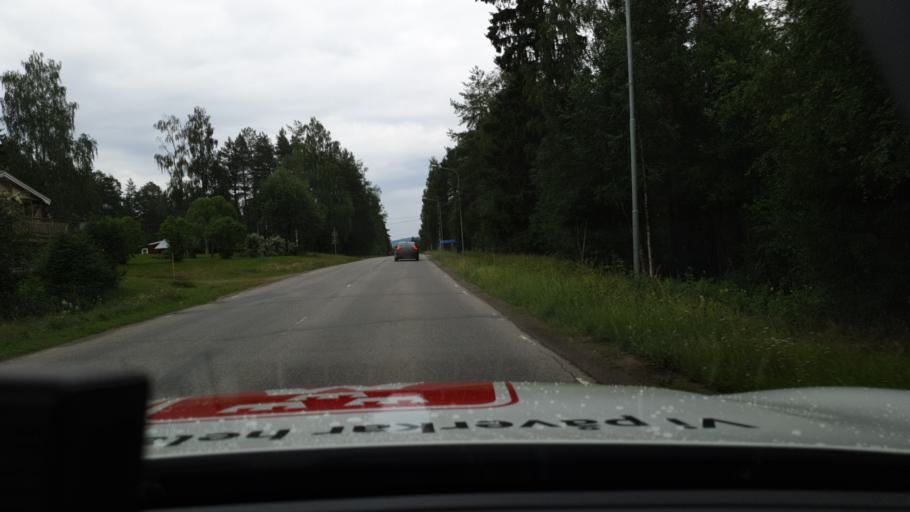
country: SE
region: Norrbotten
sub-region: Alvsbyns Kommun
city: AElvsbyn
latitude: 66.0963
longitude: 20.9432
